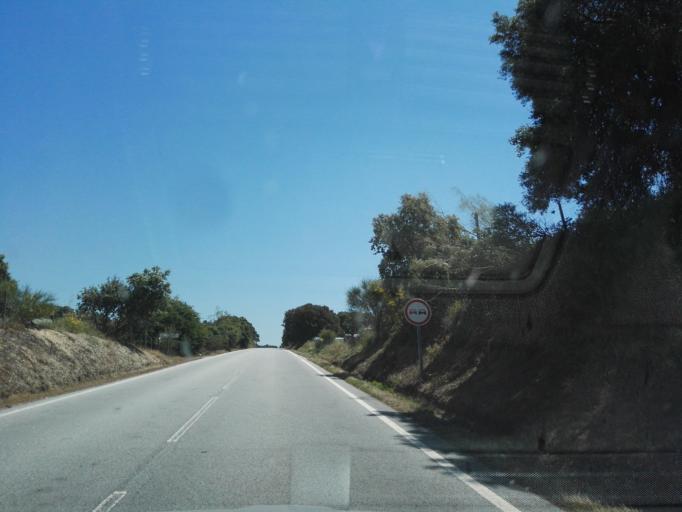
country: PT
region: Portalegre
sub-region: Elvas
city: Elvas
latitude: 38.9980
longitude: -7.1905
